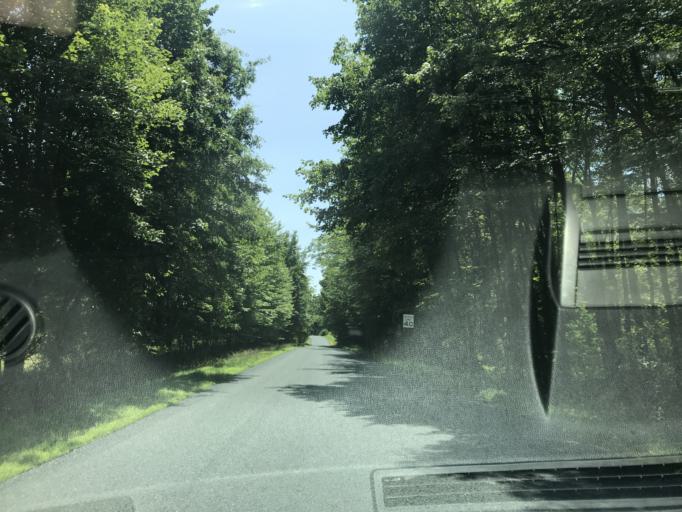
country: US
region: Maryland
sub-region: Harford County
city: Bel Air South
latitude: 39.5463
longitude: -76.2664
